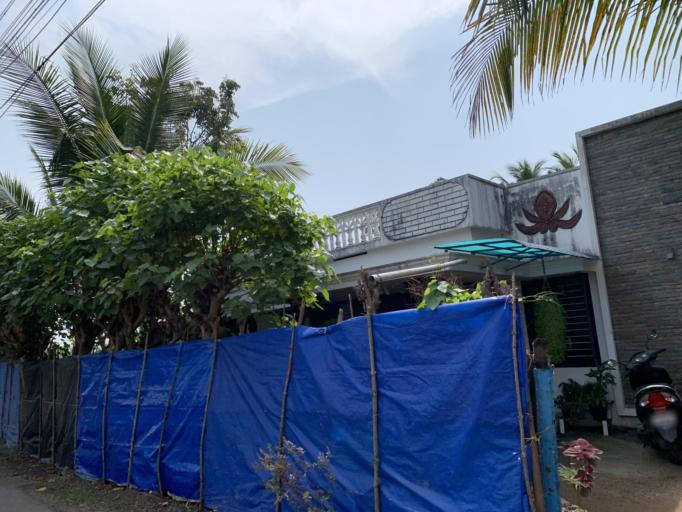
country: IN
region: Kerala
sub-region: Ernakulam
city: Cochin
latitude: 9.9131
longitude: 76.2621
